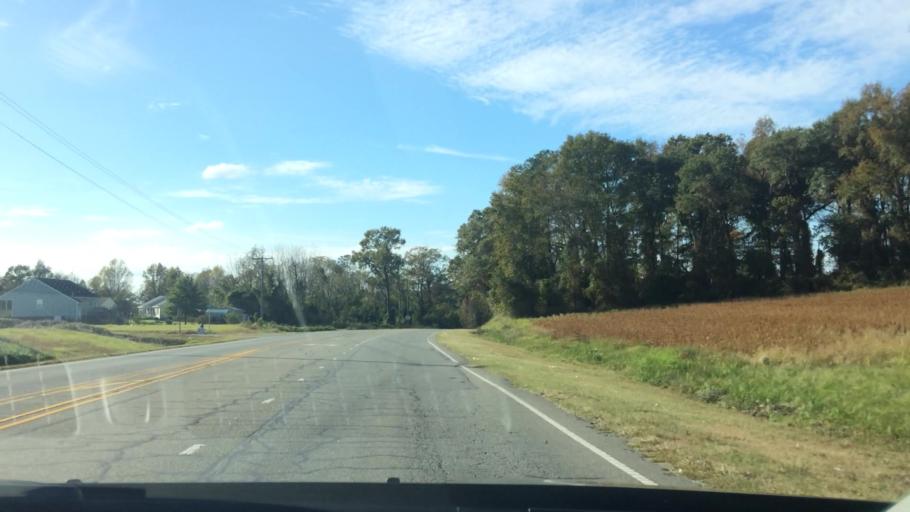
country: US
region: North Carolina
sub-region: Greene County
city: Snow Hill
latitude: 35.4563
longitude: -77.6943
